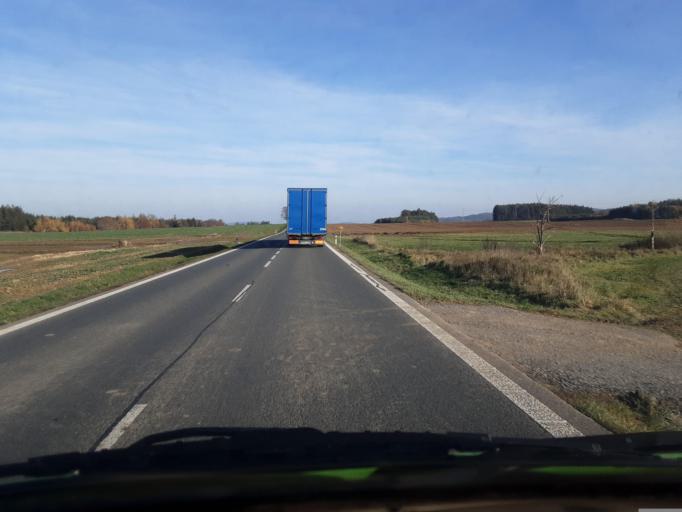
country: CZ
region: Plzensky
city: Horazd'ovice
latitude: 49.3248
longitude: 13.6119
